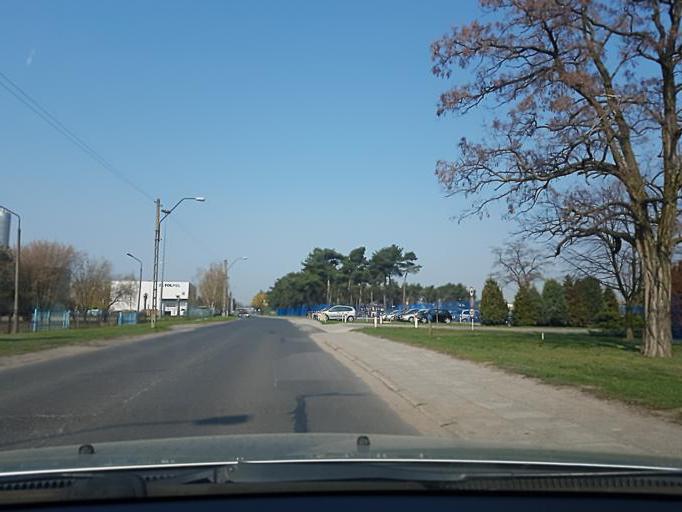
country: PL
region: Lodz Voivodeship
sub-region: Powiat kutnowski
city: Kutno
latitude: 52.2205
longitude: 19.3904
